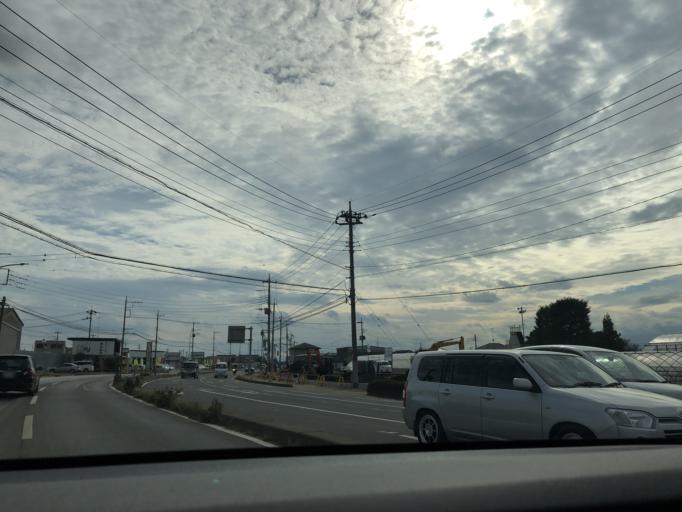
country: JP
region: Tochigi
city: Sano
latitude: 36.2961
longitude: 139.5669
